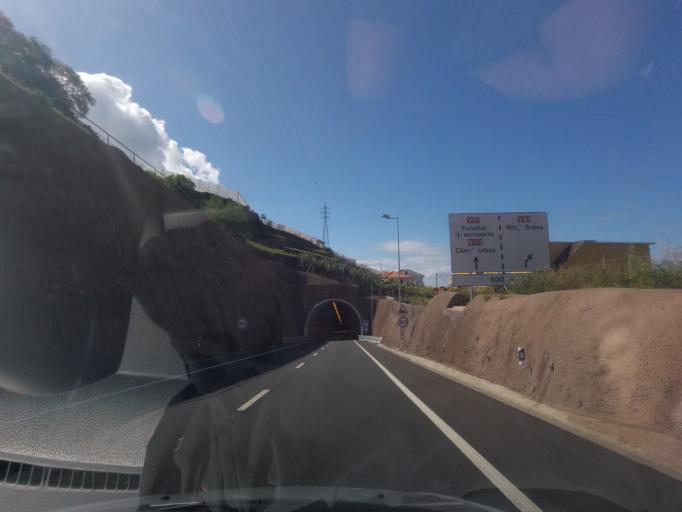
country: PT
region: Madeira
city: Camara de Lobos
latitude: 32.6666
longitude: -16.9700
